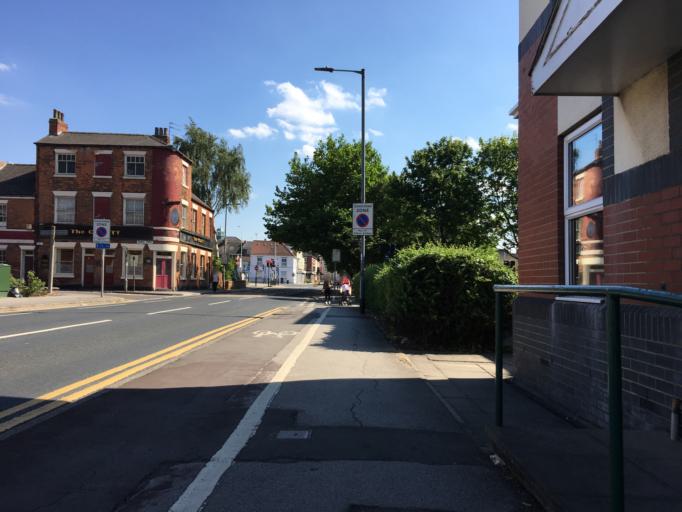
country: GB
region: England
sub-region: City of Kingston upon Hull
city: Hull
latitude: 53.7493
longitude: -0.3406
